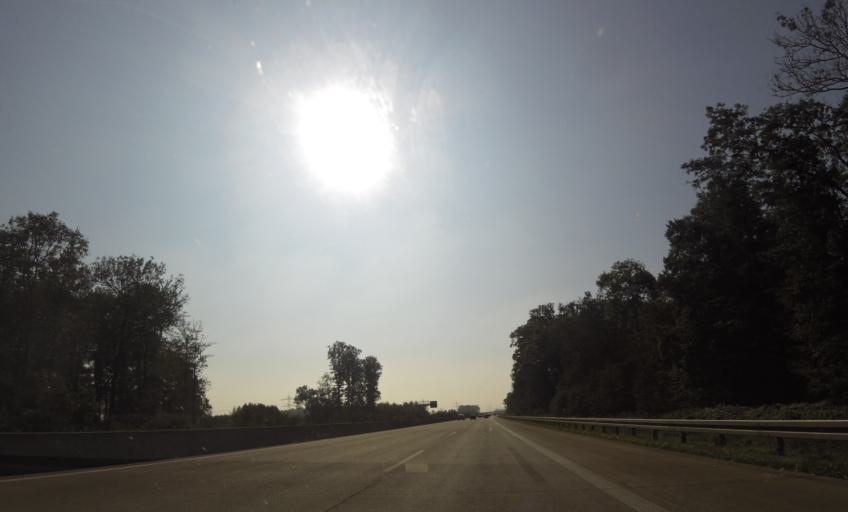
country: DE
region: Baden-Wuerttemberg
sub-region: Freiburg Region
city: Renchen
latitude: 48.6333
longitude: 8.0233
